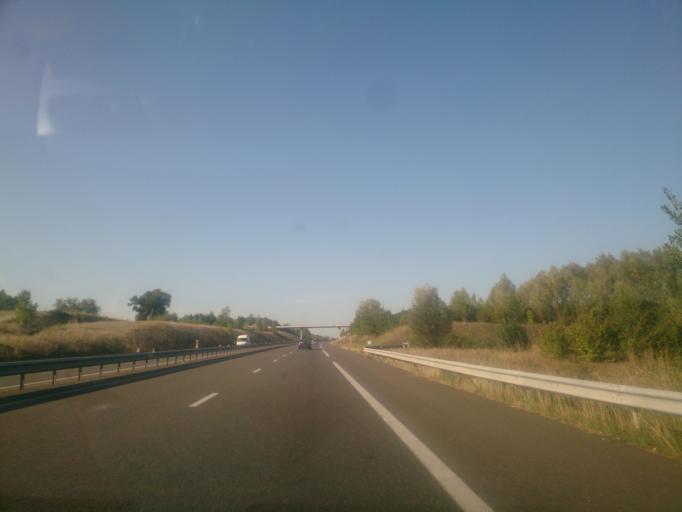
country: FR
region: Midi-Pyrenees
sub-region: Departement du Tarn-et-Garonne
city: Caussade
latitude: 44.1898
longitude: 1.5359
